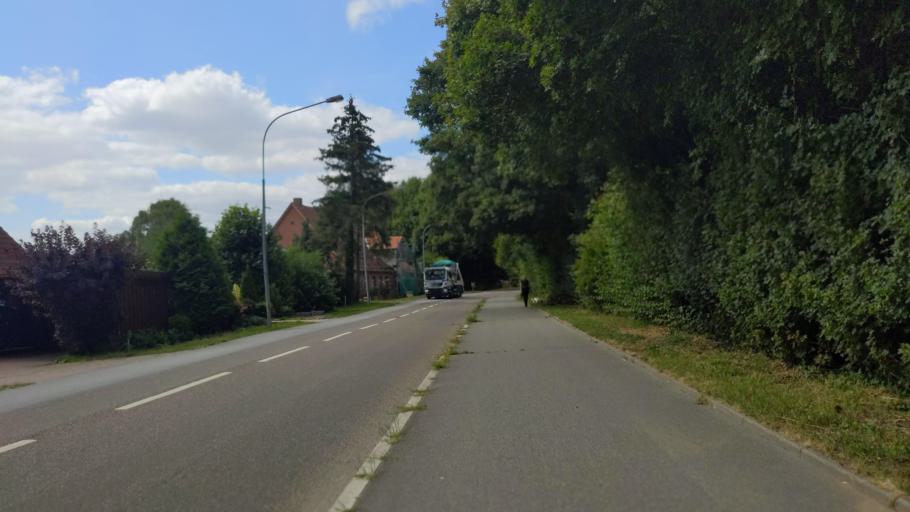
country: DE
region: Schleswig-Holstein
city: Stockelsdorf
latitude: 53.8734
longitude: 10.6162
